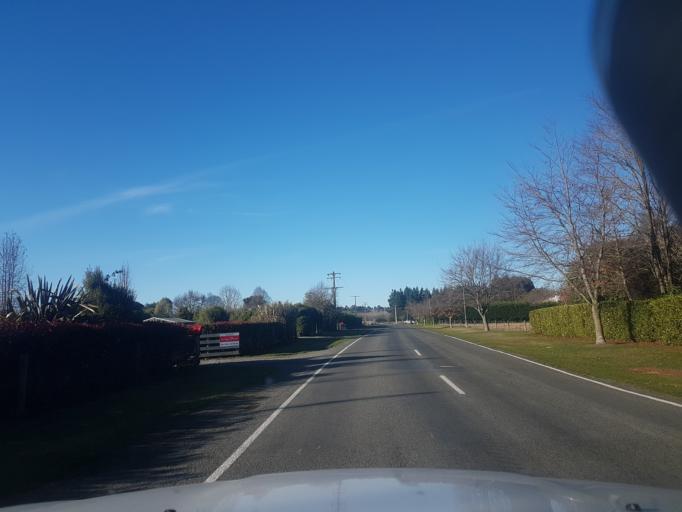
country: NZ
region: Canterbury
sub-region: Timaru District
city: Pleasant Point
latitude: -44.2564
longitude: 171.1281
